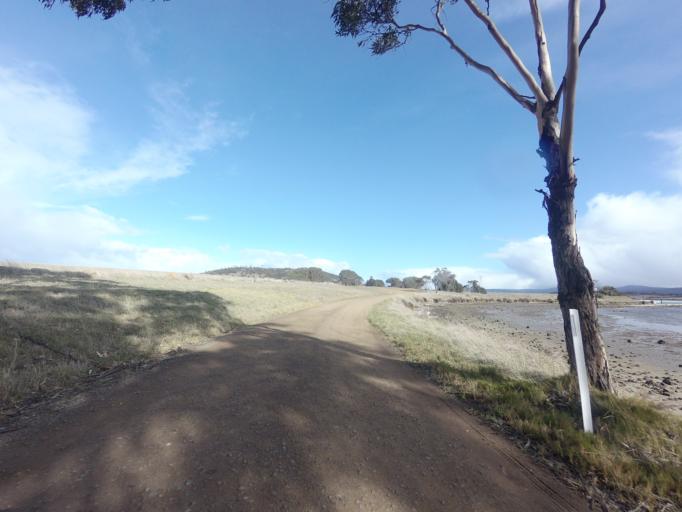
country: AU
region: Tasmania
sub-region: Sorell
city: Sorell
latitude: -42.3090
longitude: 147.9965
